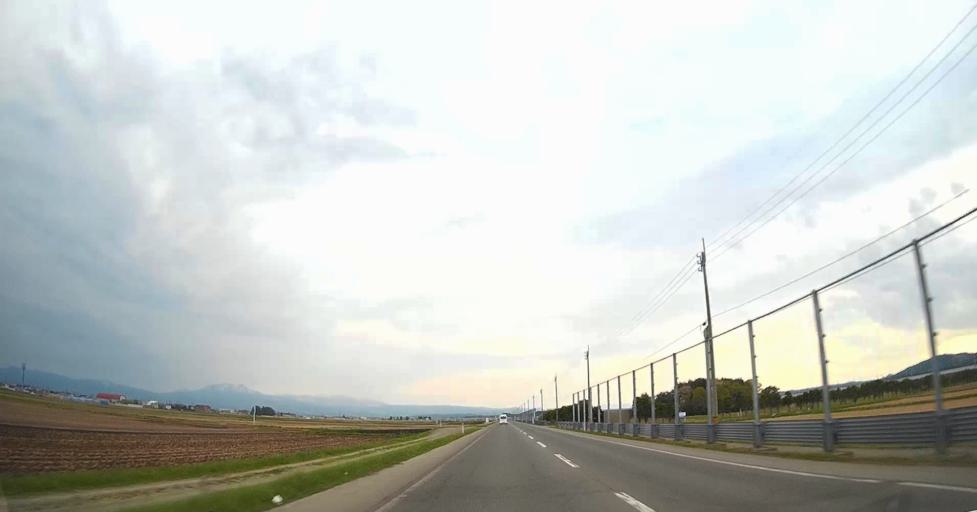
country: JP
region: Aomori
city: Aomori Shi
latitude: 40.8844
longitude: 140.6700
